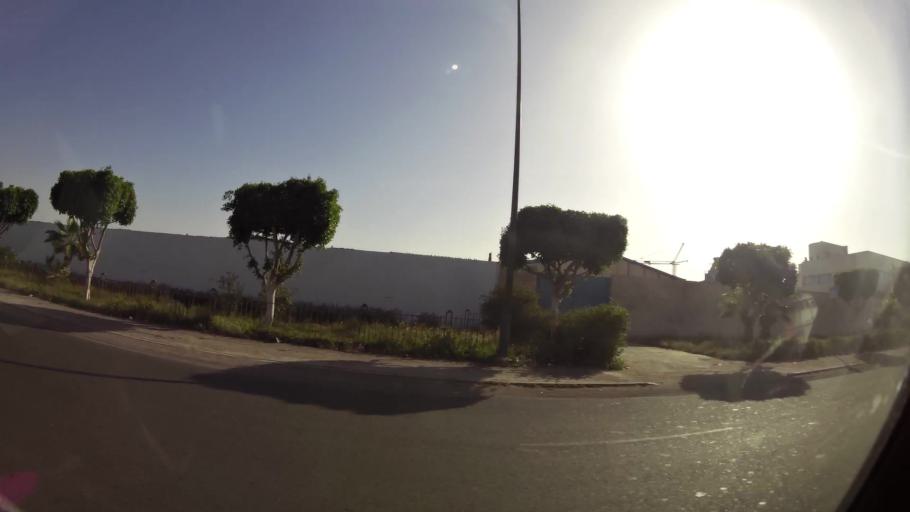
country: MA
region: Oued ed Dahab-Lagouira
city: Dakhla
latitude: 30.3920
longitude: -9.5311
